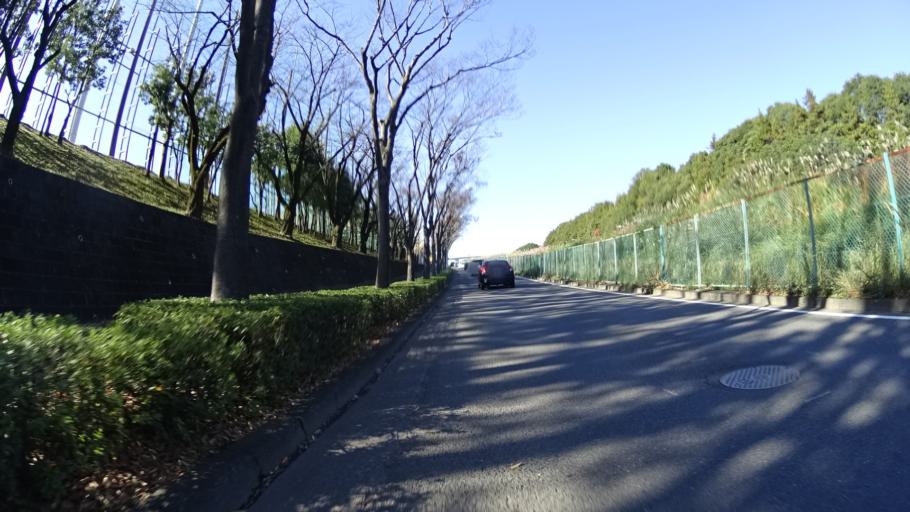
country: JP
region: Tokyo
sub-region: Machida-shi
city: Machida
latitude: 35.6106
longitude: 139.4377
